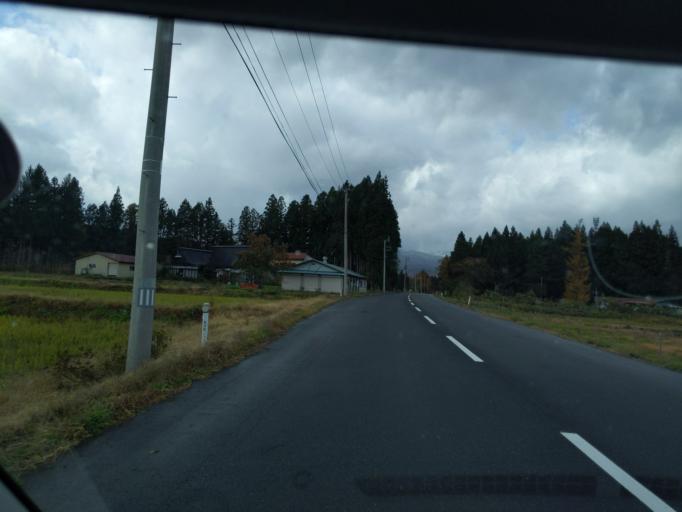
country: JP
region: Iwate
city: Mizusawa
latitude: 39.1105
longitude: 140.9648
